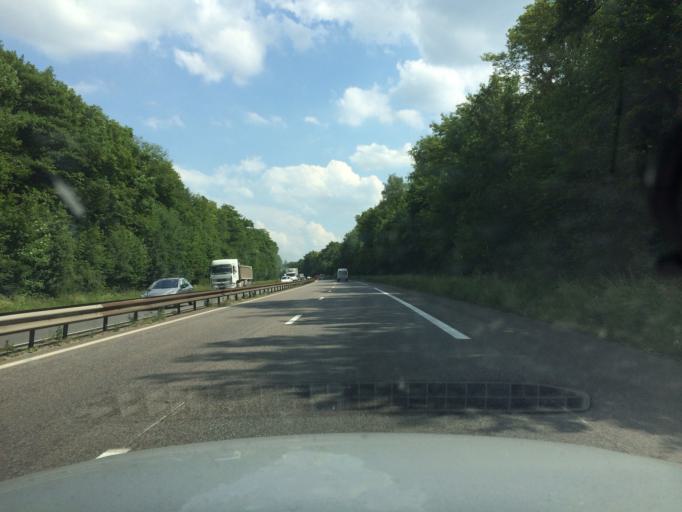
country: FR
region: Lorraine
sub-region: Departement de Meurthe-et-Moselle
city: Chavigny
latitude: 48.6534
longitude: 6.1289
